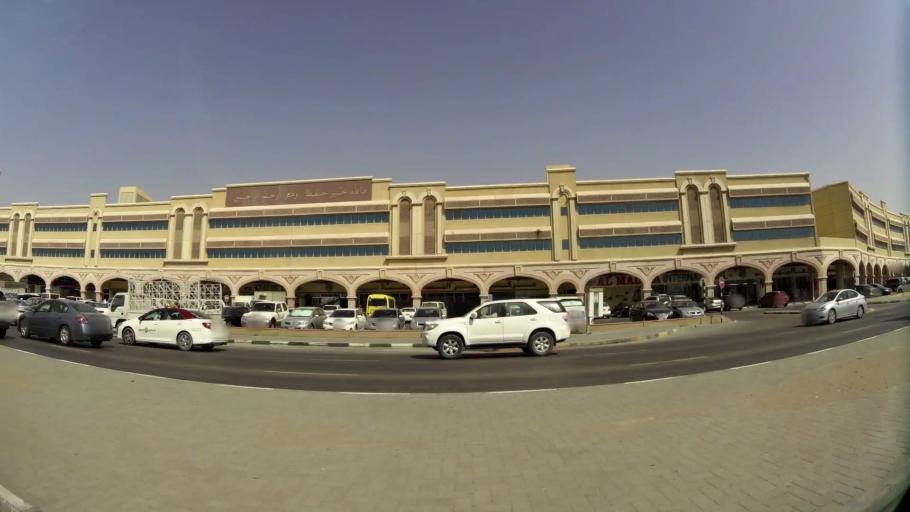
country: AE
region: Ash Shariqah
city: Sharjah
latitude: 25.3047
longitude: 55.4168
